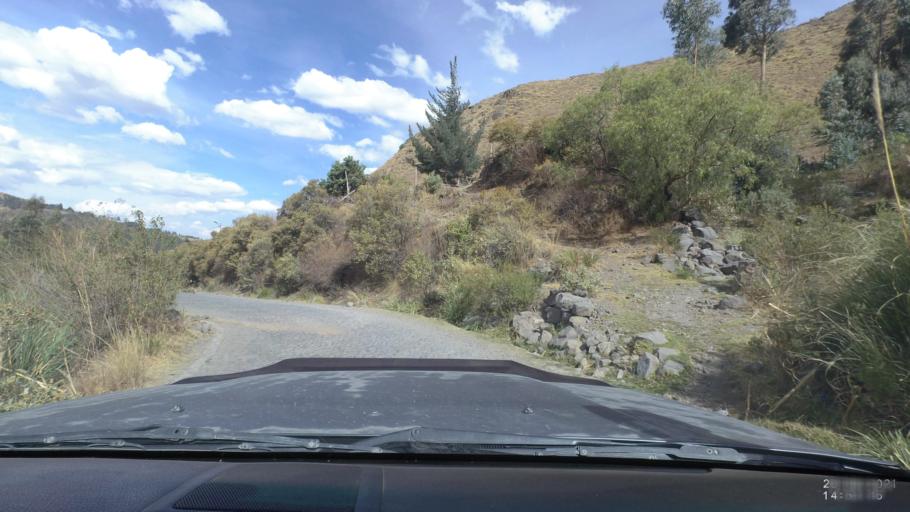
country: BO
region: Cochabamba
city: Sipe Sipe
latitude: -17.2844
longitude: -66.3076
